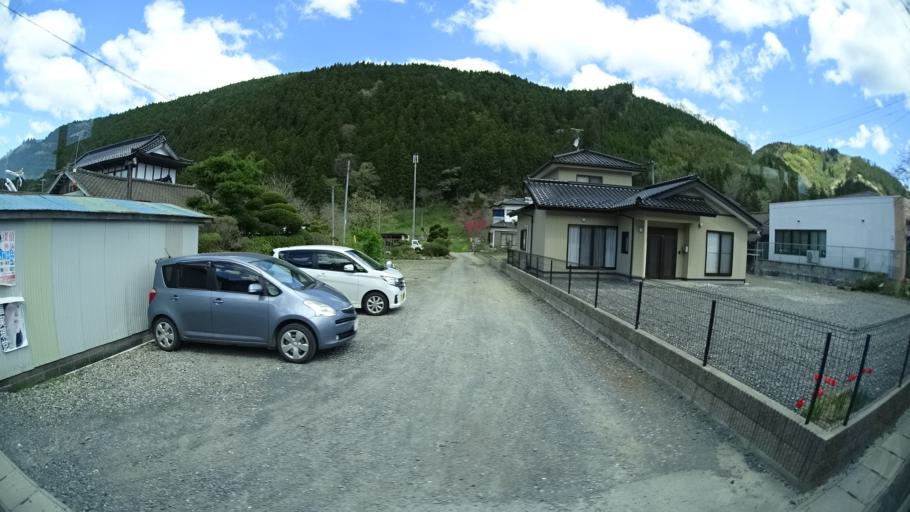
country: JP
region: Miyagi
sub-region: Oshika Gun
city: Onagawa Cho
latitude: 38.6339
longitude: 141.3582
